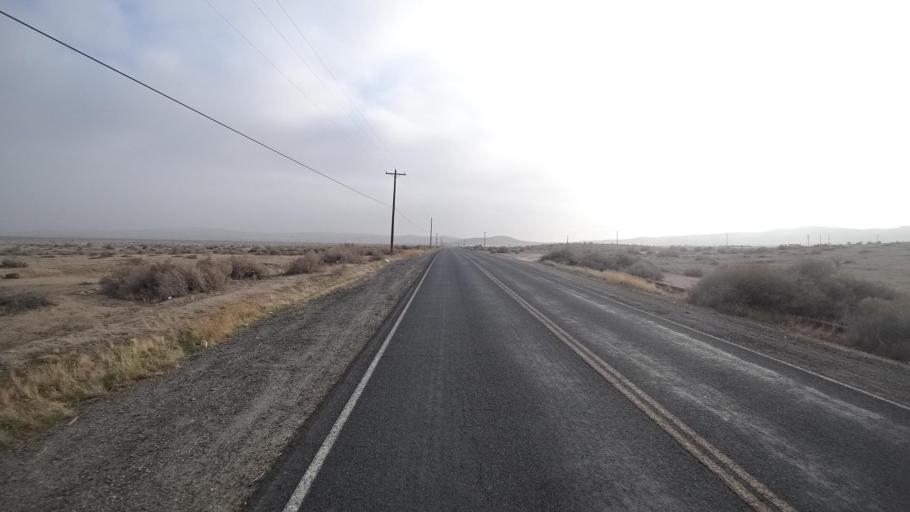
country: US
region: California
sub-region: Kern County
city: Ford City
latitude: 35.2043
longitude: -119.4456
